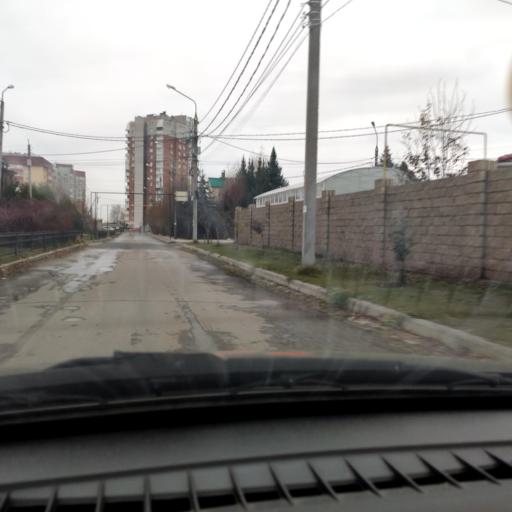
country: RU
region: Samara
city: Tol'yatti
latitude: 53.5432
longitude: 49.3730
